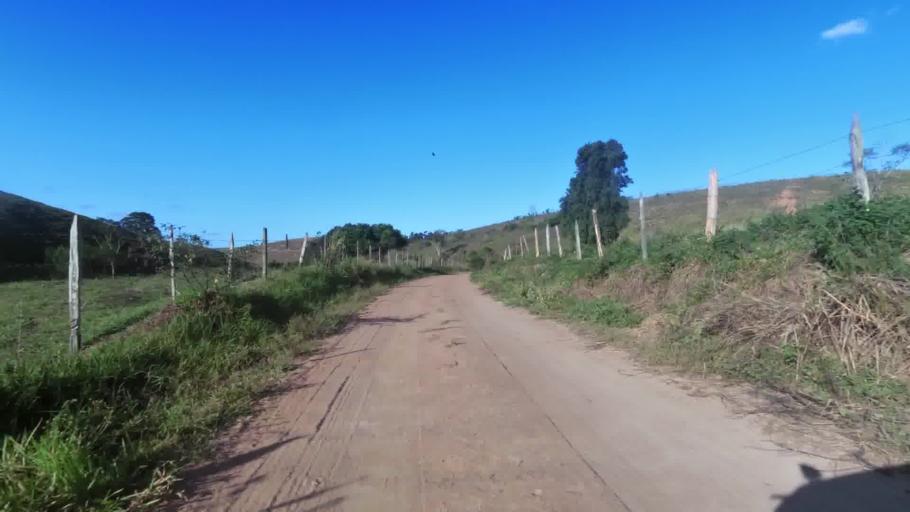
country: BR
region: Espirito Santo
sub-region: Marataizes
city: Marataizes
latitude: -21.1427
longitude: -41.0238
